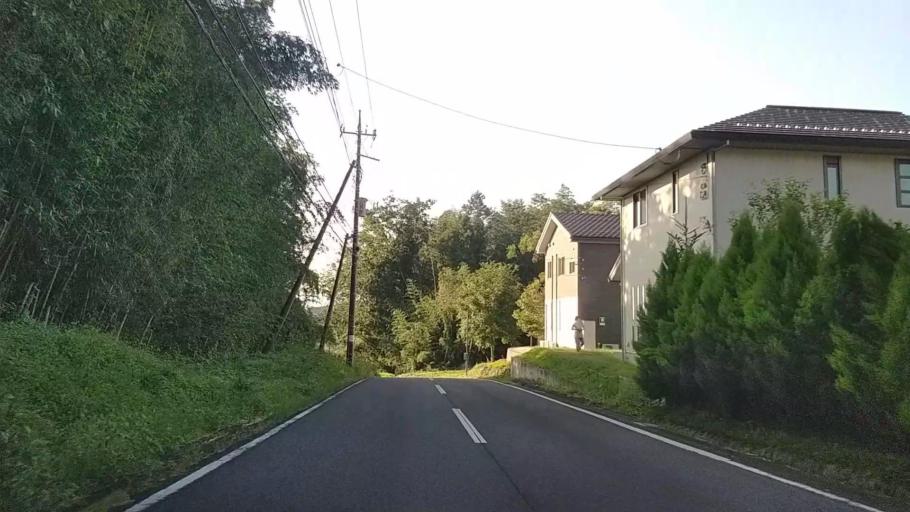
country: JP
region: Gunma
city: Annaka
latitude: 36.3565
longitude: 138.8561
